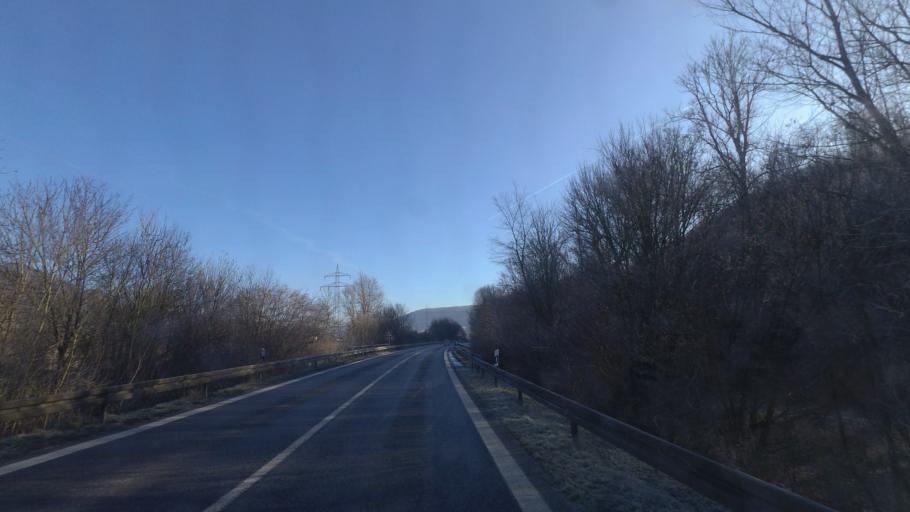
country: DE
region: Bavaria
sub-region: Regierungsbezirk Mittelfranken
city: Greding
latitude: 49.0000
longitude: 11.3686
